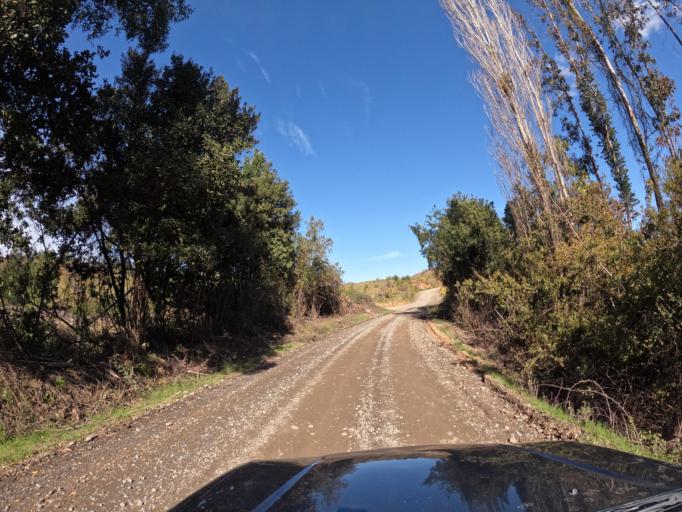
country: CL
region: Biobio
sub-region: Provincia de Biobio
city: La Laja
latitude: -37.0813
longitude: -72.8344
